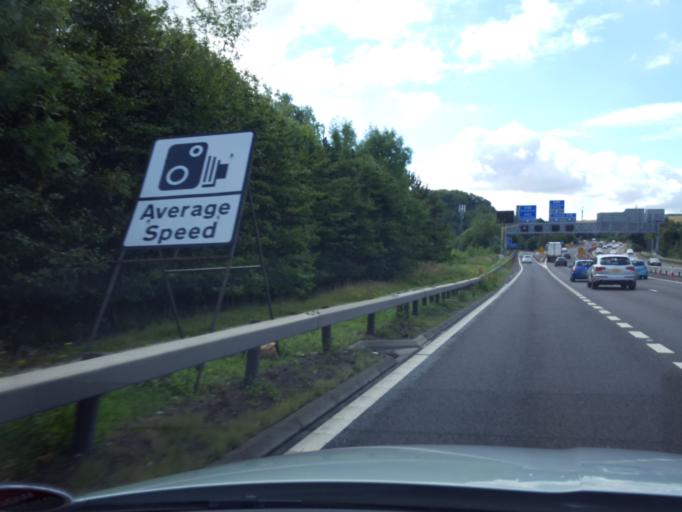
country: GB
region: Scotland
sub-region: Fife
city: Inverkeithing
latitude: 56.0402
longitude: -3.4063
